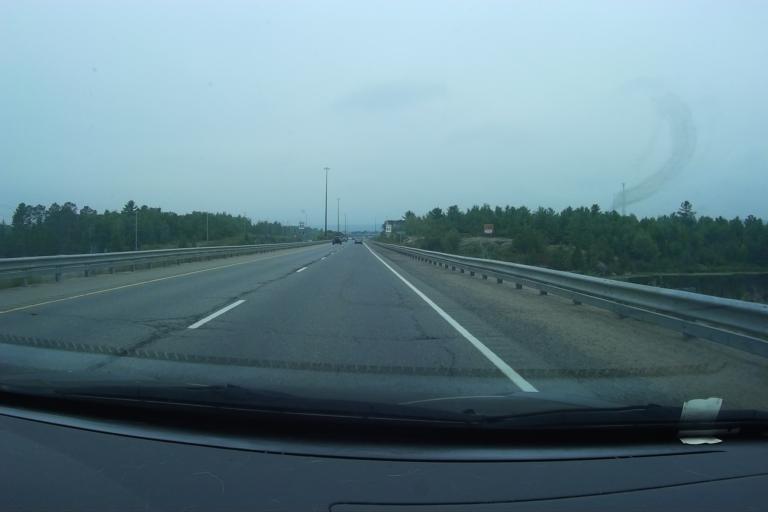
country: CA
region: Ontario
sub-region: Nipissing District
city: North Bay
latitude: 46.2982
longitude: -79.4264
